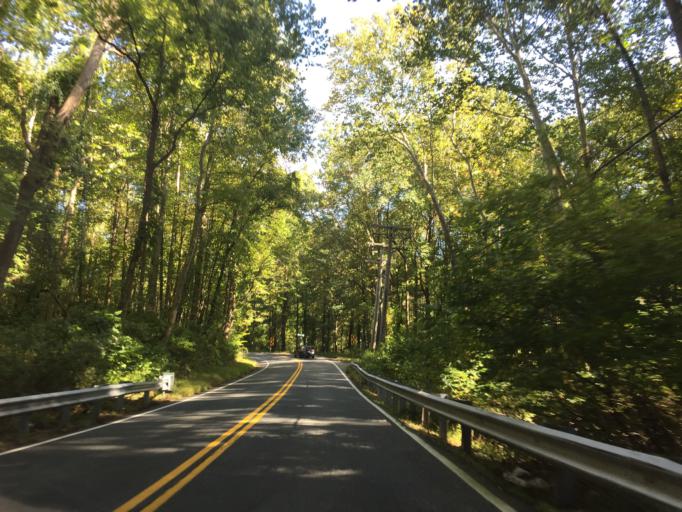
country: US
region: Maryland
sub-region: Harford County
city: Fallston
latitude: 39.5532
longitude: -76.4315
